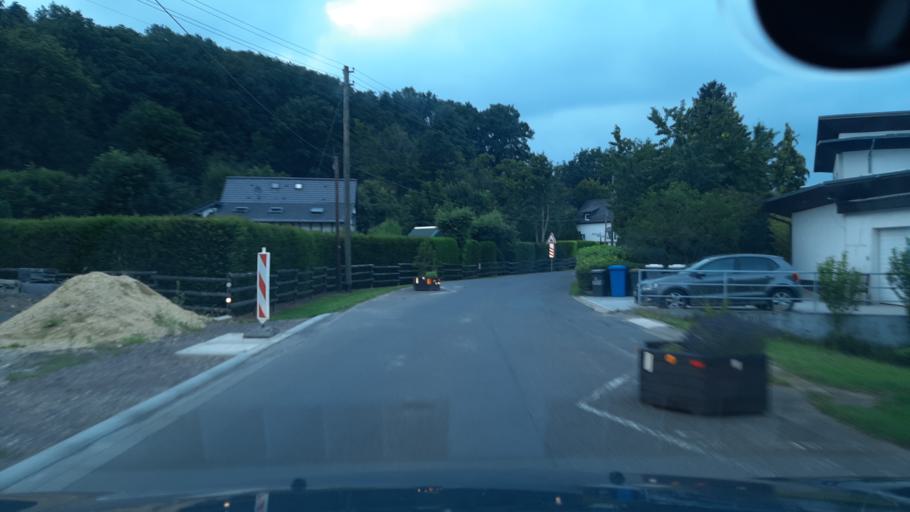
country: DE
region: North Rhine-Westphalia
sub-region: Regierungsbezirk Koln
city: Mechernich
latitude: 50.6011
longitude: 6.6820
